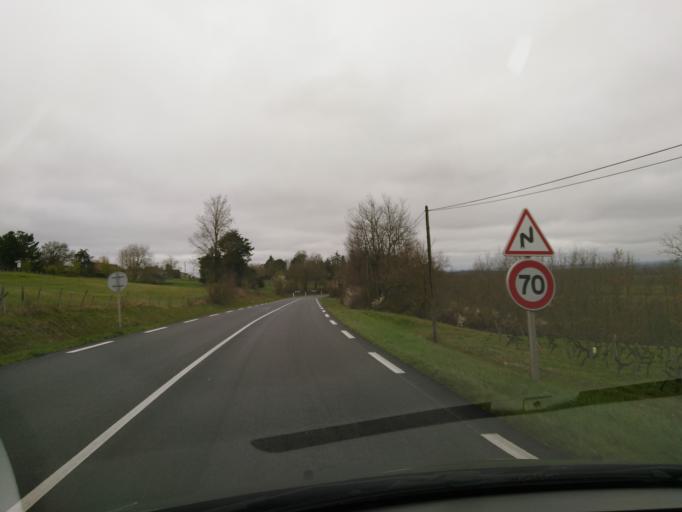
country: FR
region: Aquitaine
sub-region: Departement de la Dordogne
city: Monbazillac
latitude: 44.7378
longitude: 0.5419
